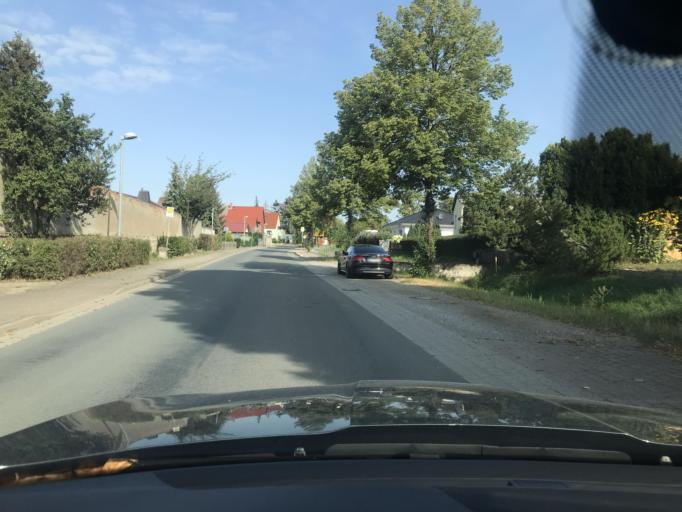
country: DE
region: Saxony-Anhalt
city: Gross Quenstedt
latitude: 51.9300
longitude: 11.1190
